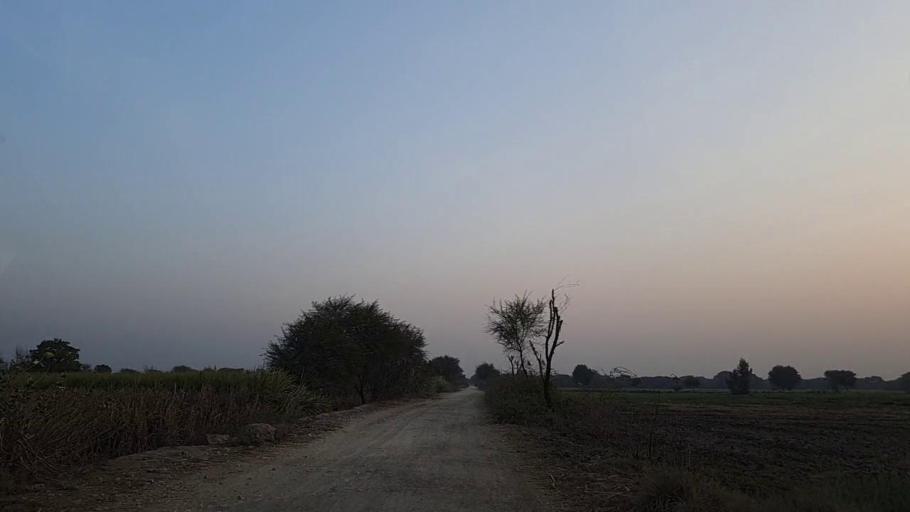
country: PK
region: Sindh
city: Tando Ghulam Ali
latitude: 25.1559
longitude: 68.9369
